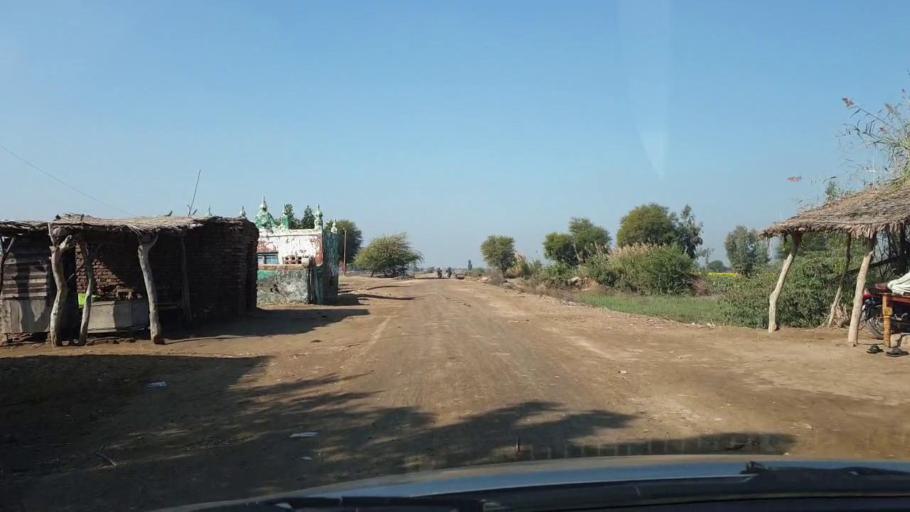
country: PK
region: Sindh
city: Jhol
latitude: 25.8807
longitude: 68.9218
